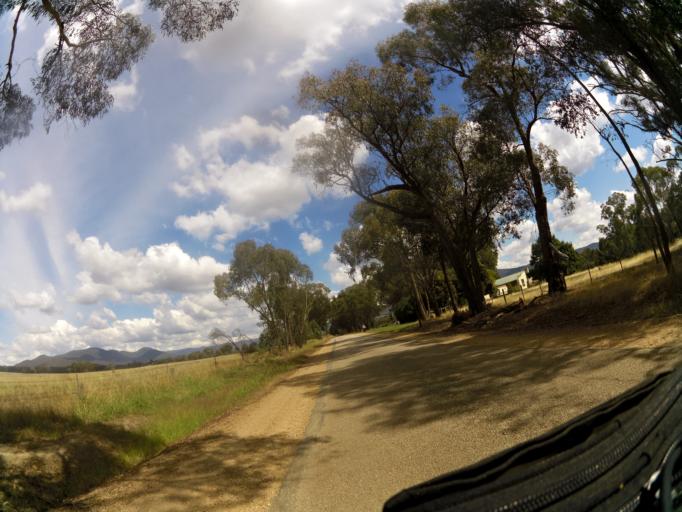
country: AU
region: Victoria
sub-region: Benalla
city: Benalla
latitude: -36.7529
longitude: 145.9803
